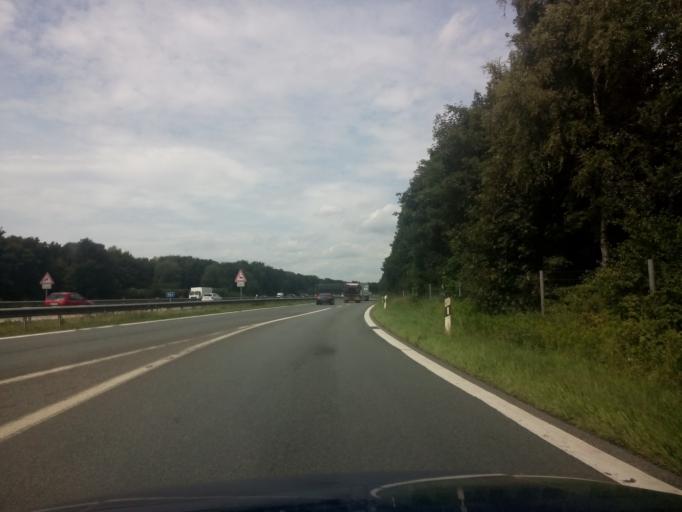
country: DE
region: Lower Saxony
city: Ritterhude
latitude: 53.1489
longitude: 8.7315
